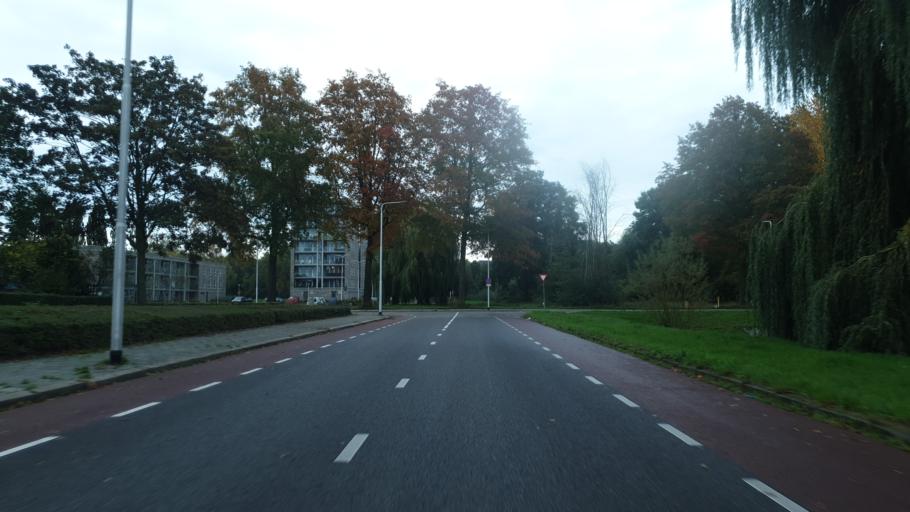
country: NL
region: Gelderland
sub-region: Gemeente Nijmegen
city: Lindenholt
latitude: 51.8058
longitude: 5.8110
